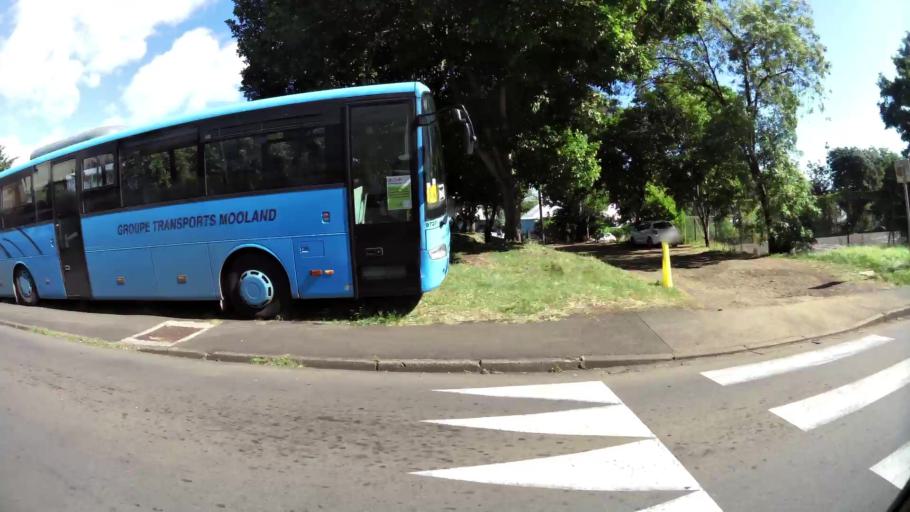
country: RE
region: Reunion
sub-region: Reunion
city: Saint-Denis
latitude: -20.8971
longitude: 55.4868
